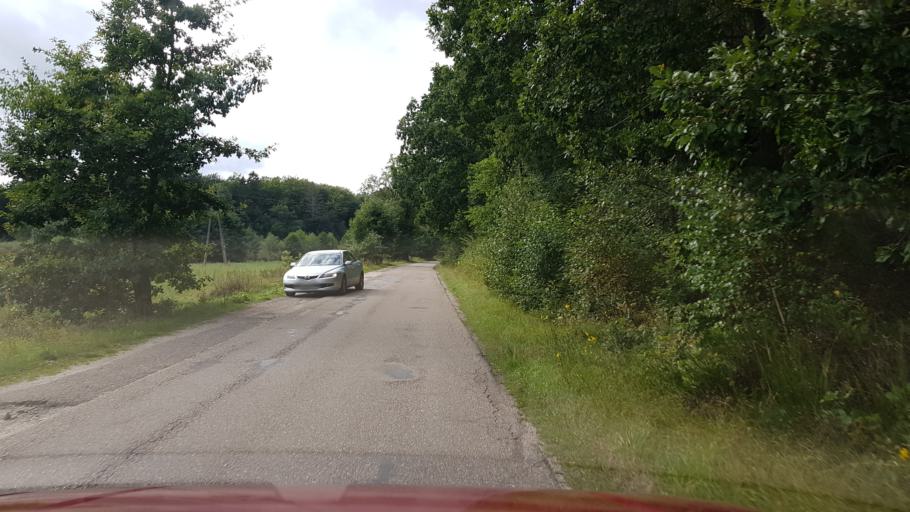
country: PL
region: West Pomeranian Voivodeship
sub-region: Powiat bialogardzki
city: Tychowo
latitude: 54.0229
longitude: 16.3702
